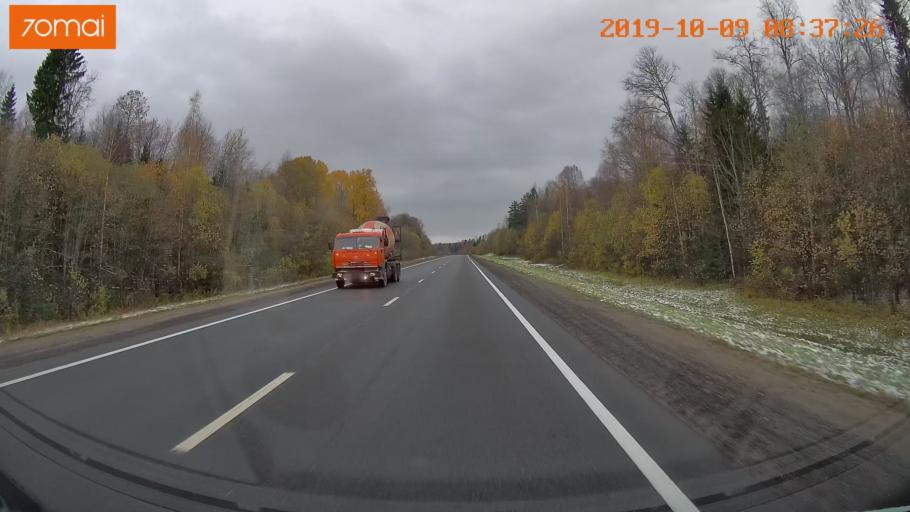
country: RU
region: Vologda
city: Gryazovets
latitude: 58.9413
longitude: 40.1745
